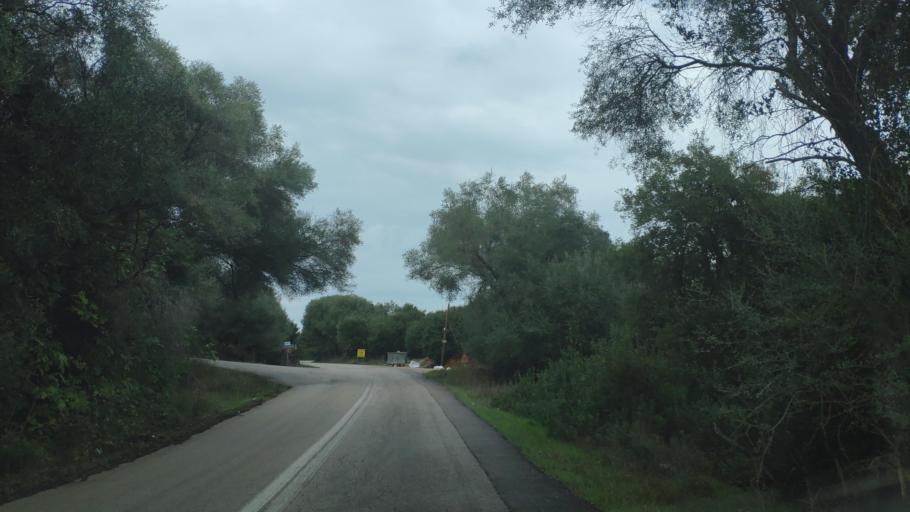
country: GR
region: West Greece
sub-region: Nomos Aitolias kai Akarnanias
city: Vonitsa
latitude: 38.9248
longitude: 20.8602
